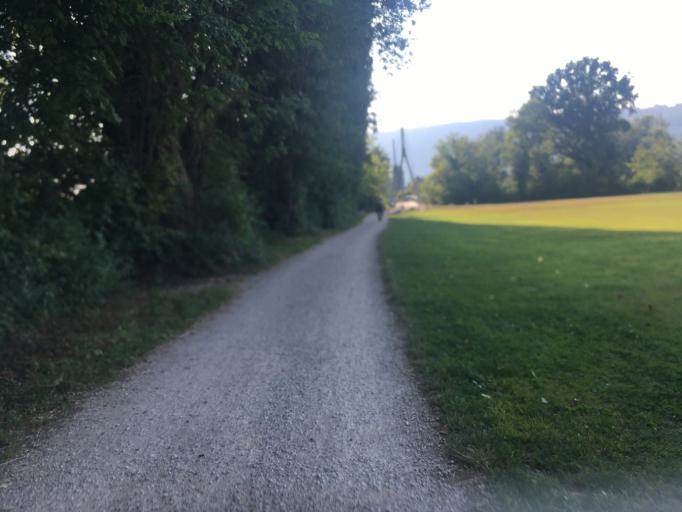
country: CH
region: Bern
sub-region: Biel/Bienne District
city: Bellmund
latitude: 47.1195
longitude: 7.2562
